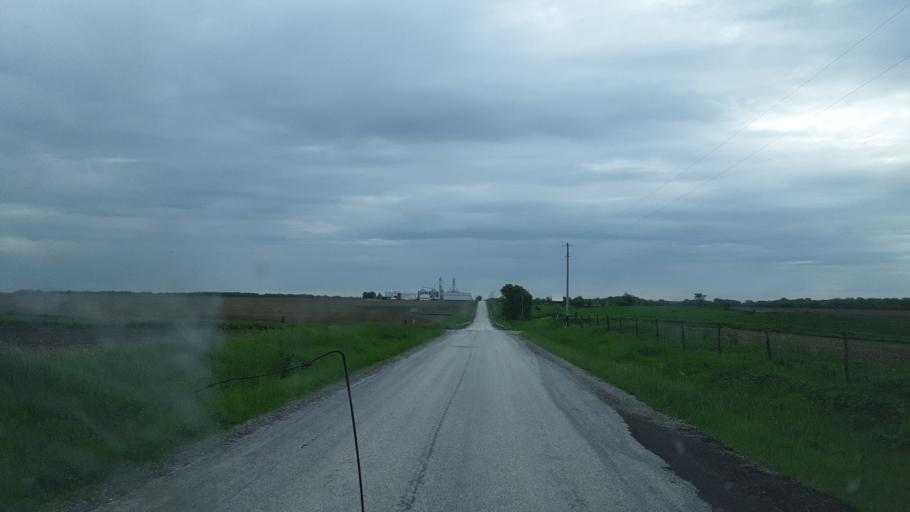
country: US
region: Illinois
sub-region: McDonough County
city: Macomb
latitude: 40.3817
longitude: -90.6298
